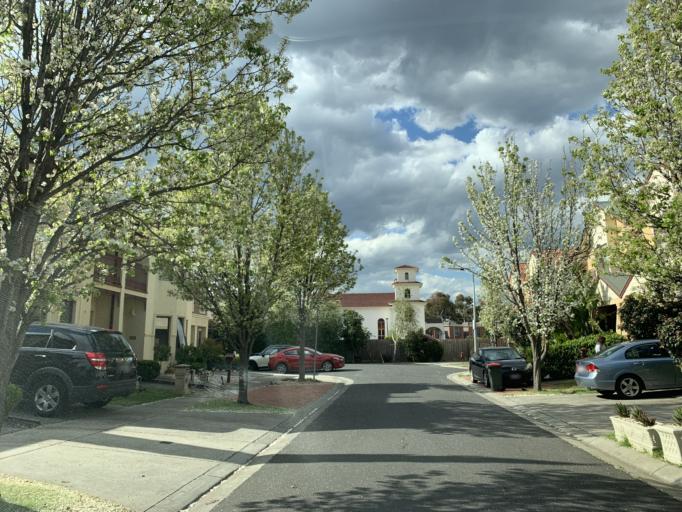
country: AU
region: Victoria
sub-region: Moonee Valley
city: Keilor East
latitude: -37.7502
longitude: 144.8596
